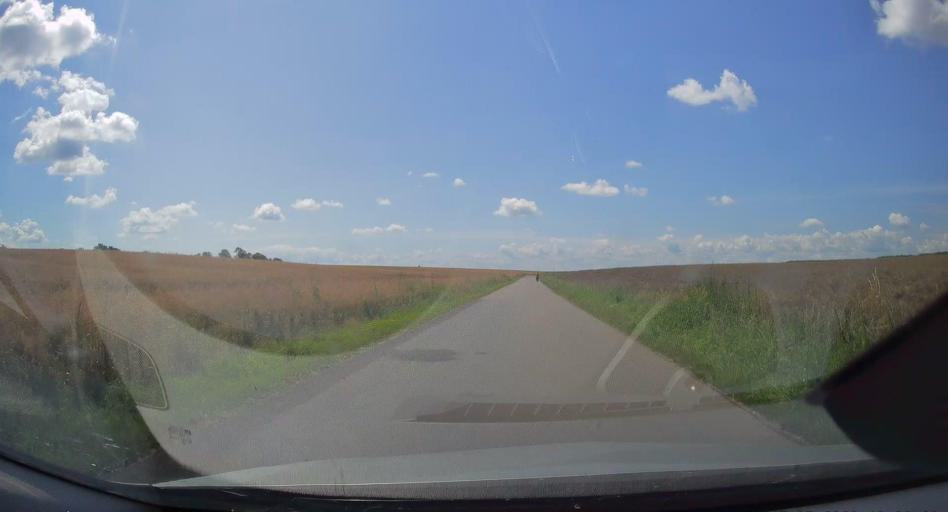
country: PL
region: Subcarpathian Voivodeship
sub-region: Powiat jaroslawski
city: Sosnica
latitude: 49.8594
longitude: 22.8810
